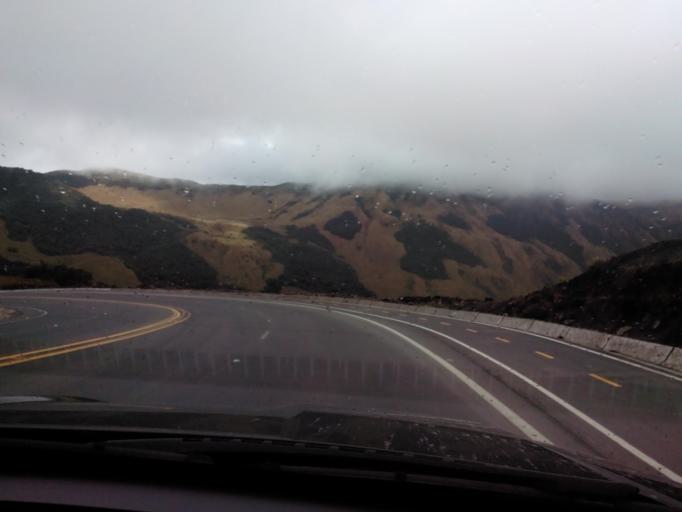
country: EC
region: Pichincha
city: Sangolqui
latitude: -0.3395
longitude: -78.2140
